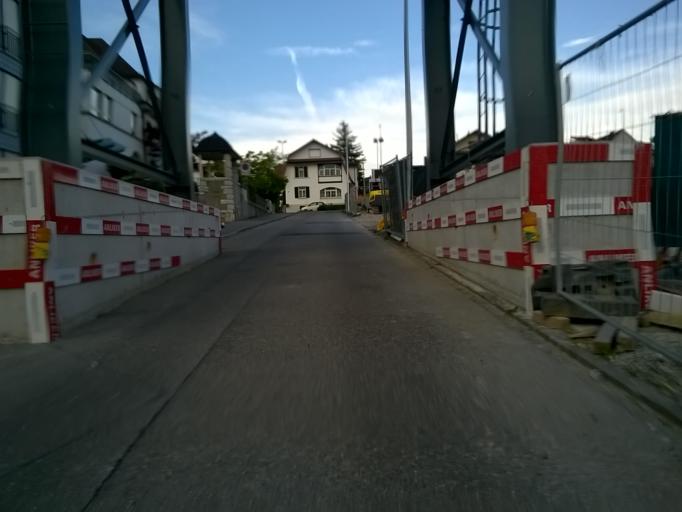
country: CH
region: Zurich
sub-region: Bezirk Uster
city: Duebendorf / Kunklerstrasse
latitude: 47.3985
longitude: 8.6233
